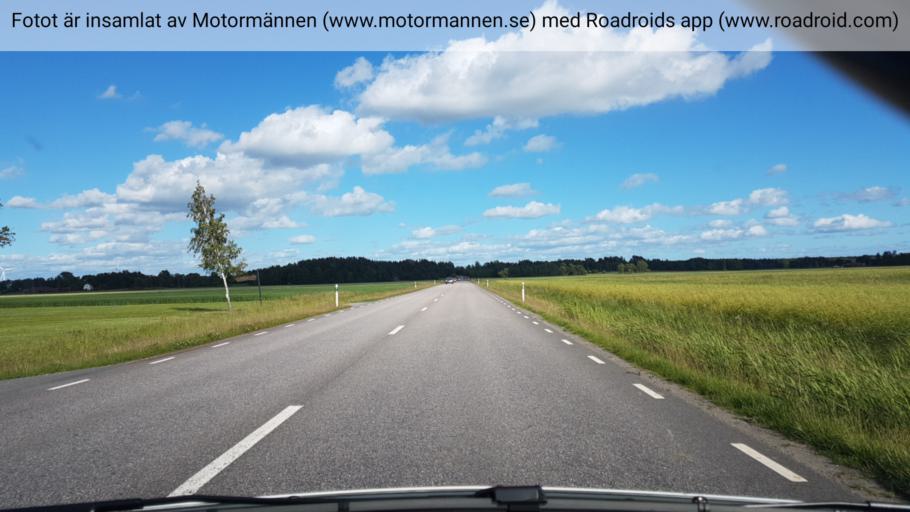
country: SE
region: Vaestra Goetaland
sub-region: Grastorps Kommun
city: Graestorp
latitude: 58.3260
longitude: 12.7311
